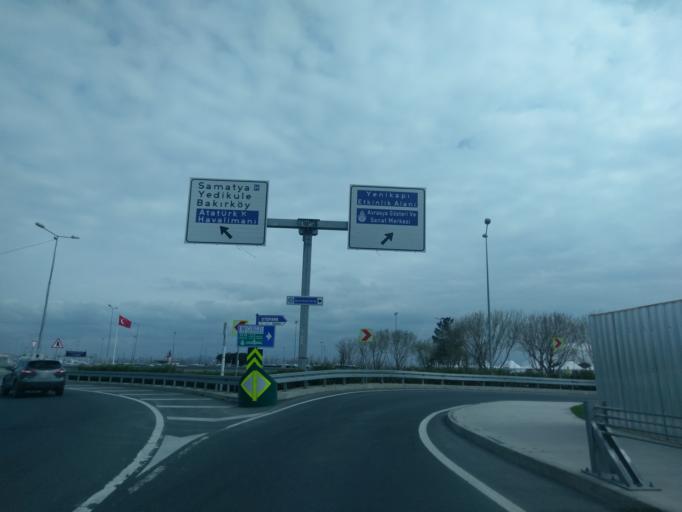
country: TR
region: Istanbul
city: Istanbul
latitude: 41.0013
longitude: 28.9427
